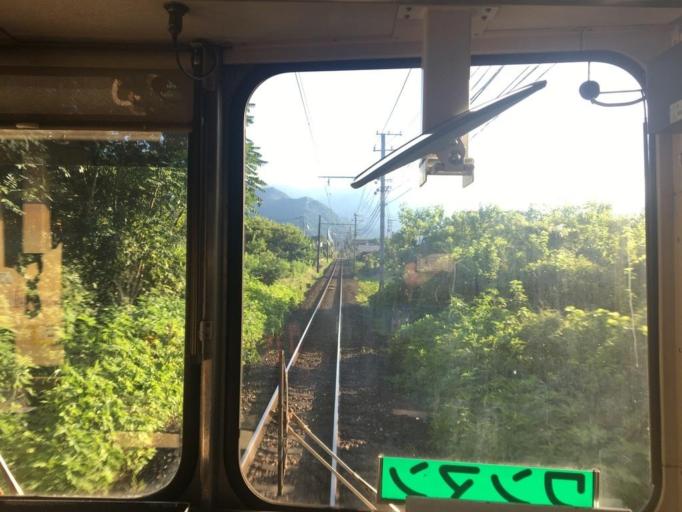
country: JP
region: Saitama
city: Chichibu
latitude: 35.9763
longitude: 139.0735
